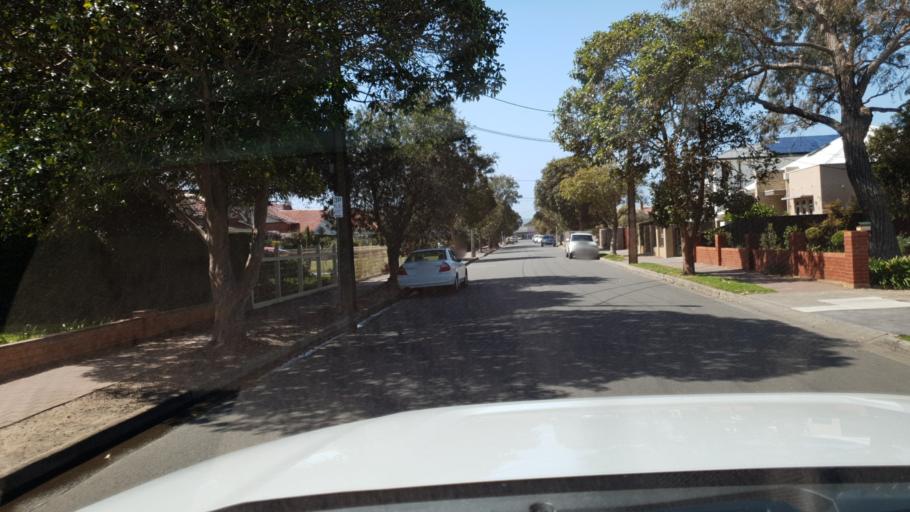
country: AU
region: South Australia
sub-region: Adelaide
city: Brighton
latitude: -35.0210
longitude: 138.5201
